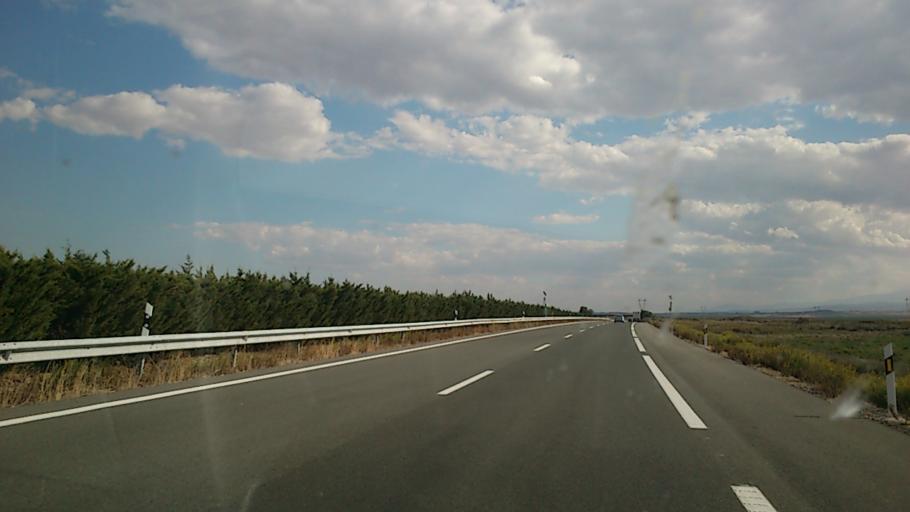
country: ES
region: La Rioja
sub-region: Provincia de La Rioja
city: Rincon de Soto
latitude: 42.1838
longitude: -1.8400
